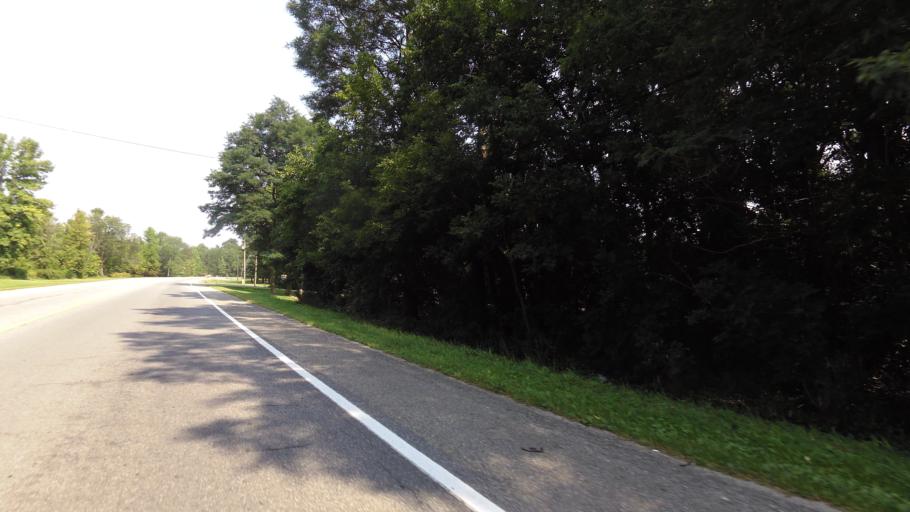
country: CA
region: Ontario
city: Brockville
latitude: 44.6159
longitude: -75.6469
